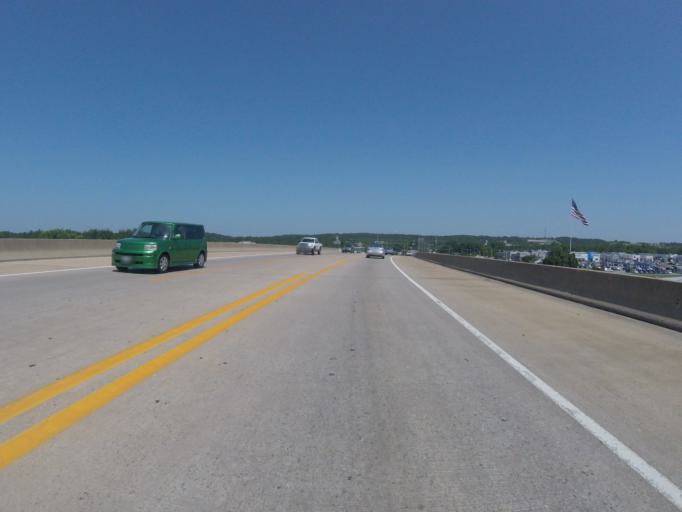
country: US
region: Arkansas
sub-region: Washington County
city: Johnson
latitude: 36.1054
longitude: -94.1797
